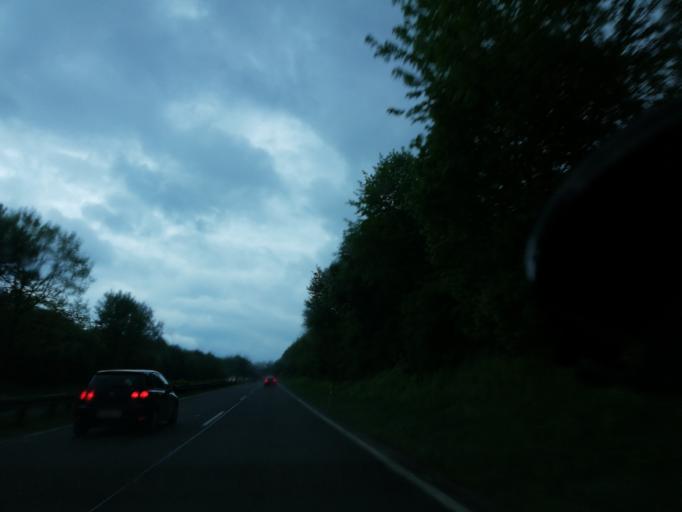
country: DE
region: North Rhine-Westphalia
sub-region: Regierungsbezirk Dusseldorf
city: Wuppertal
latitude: 51.2350
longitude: 7.1559
